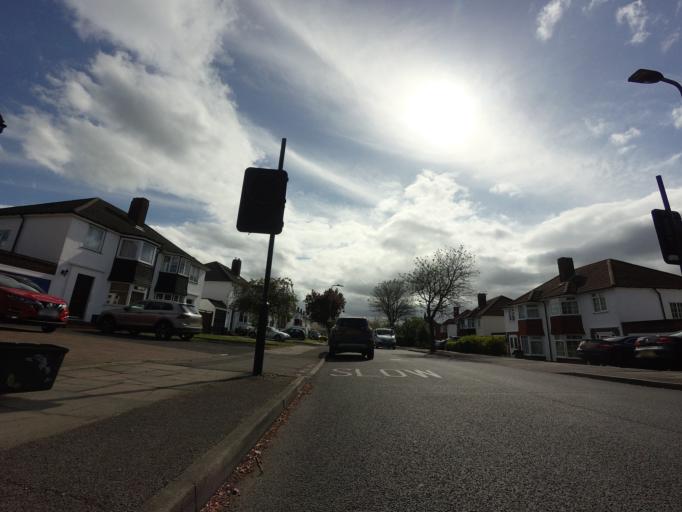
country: GB
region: England
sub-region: Greater London
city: Orpington
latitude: 51.3737
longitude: 0.1155
